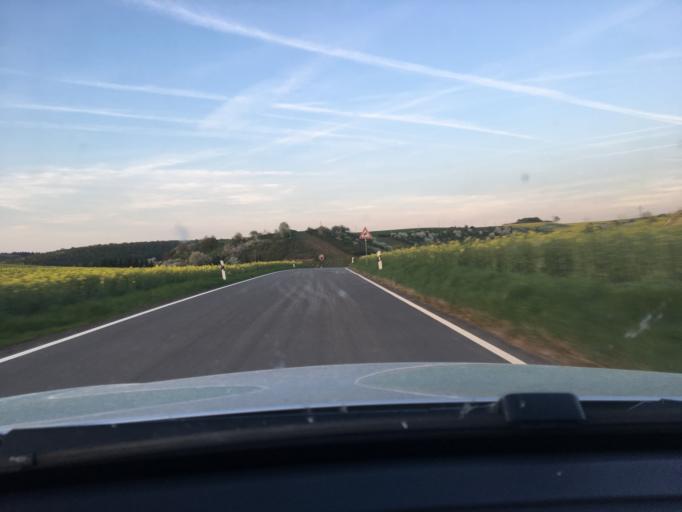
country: DE
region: Rheinland-Pfalz
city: Kalkofen
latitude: 49.7290
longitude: 7.8323
